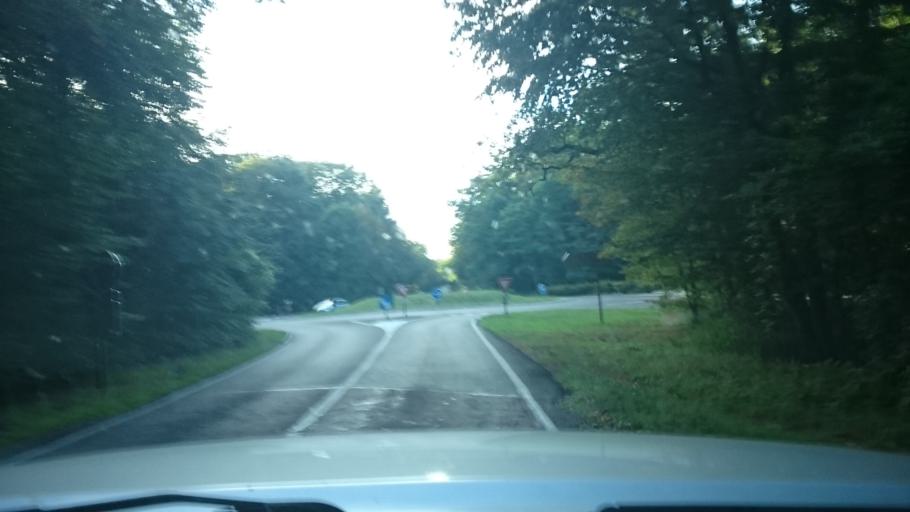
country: FR
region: Ile-de-France
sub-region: Departement de Seine-et-Marne
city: Samoreau
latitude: 48.4047
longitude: 2.7532
